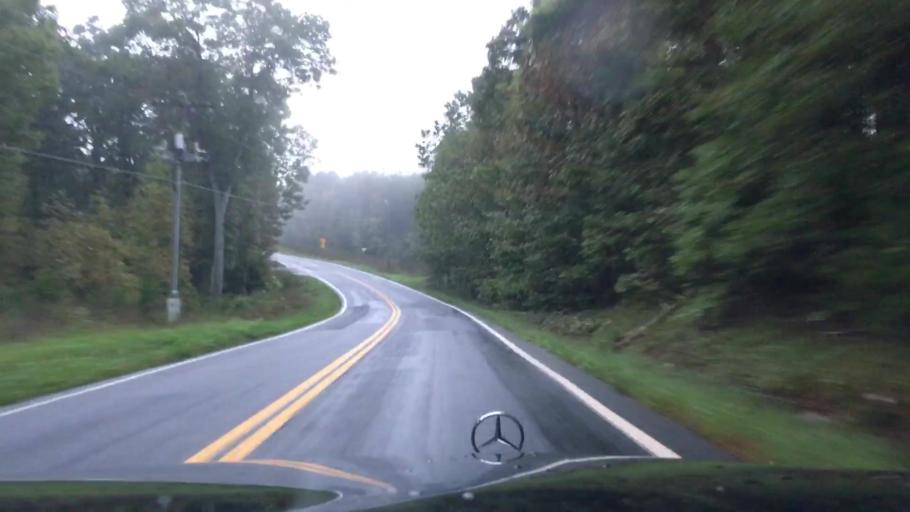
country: US
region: Virginia
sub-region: Campbell County
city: Timberlake
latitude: 37.2523
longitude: -79.2792
